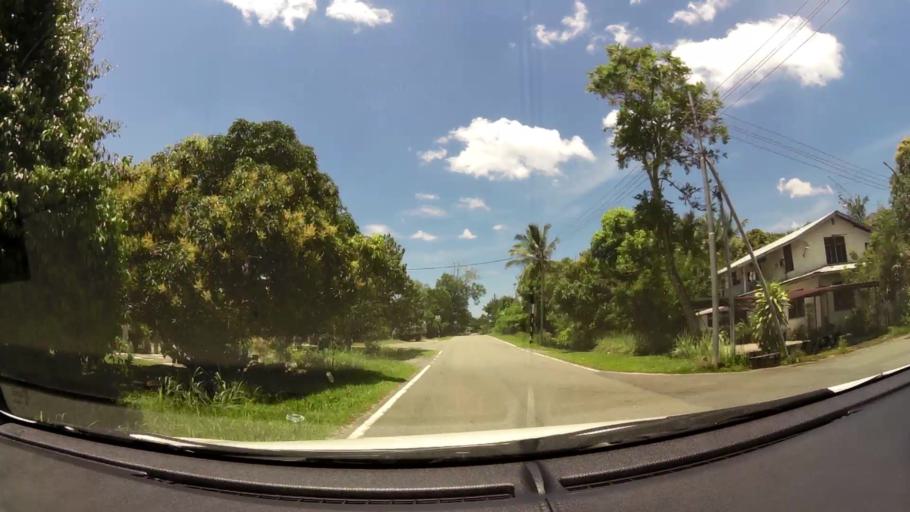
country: BN
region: Brunei and Muara
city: Bandar Seri Begawan
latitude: 4.9424
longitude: 114.9569
